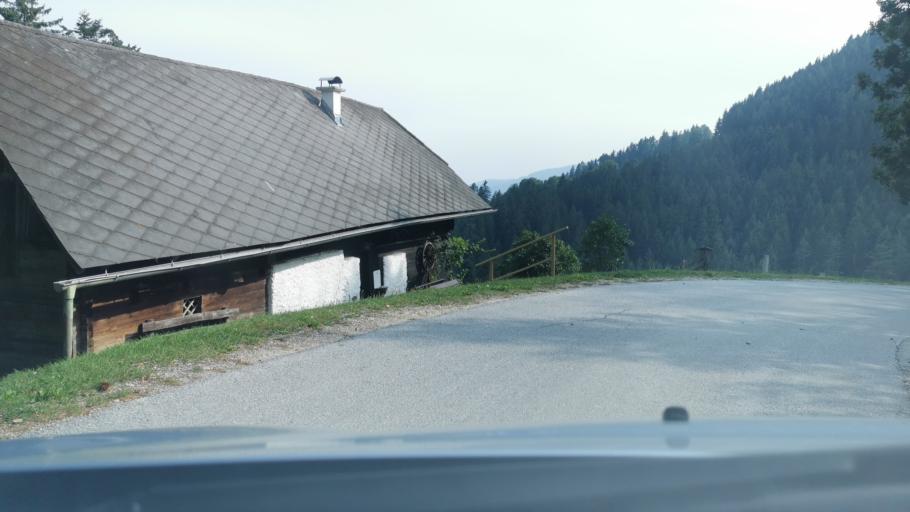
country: AT
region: Styria
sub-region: Politischer Bezirk Weiz
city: Fischbach
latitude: 47.3978
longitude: 15.6444
